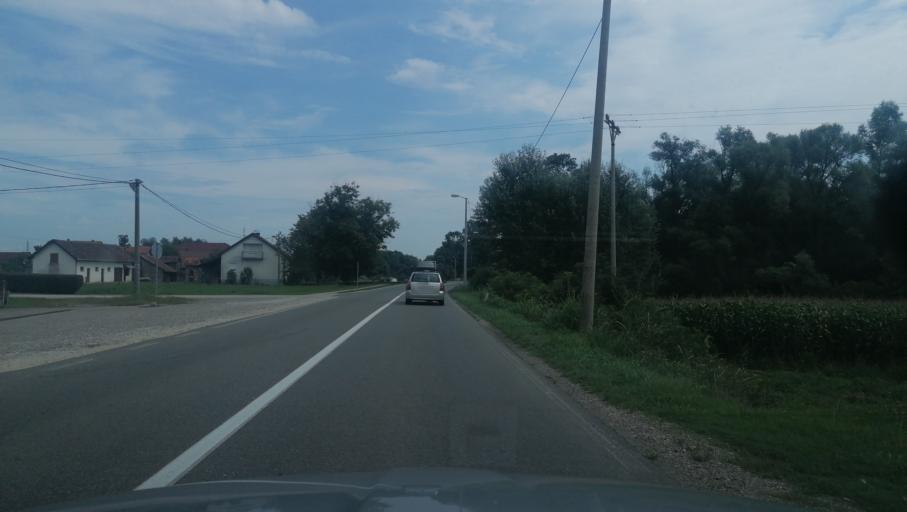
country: BA
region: Brcko
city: Brcko
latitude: 44.9265
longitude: 18.7307
